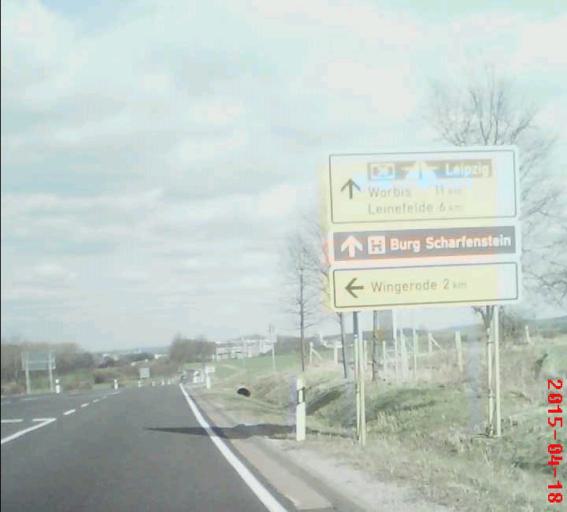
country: DE
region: Thuringia
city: Wingerode
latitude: 51.3796
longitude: 10.2416
